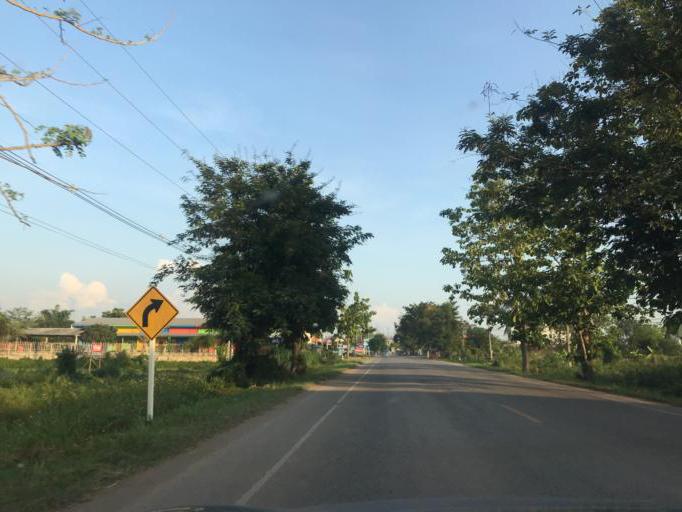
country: TH
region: Phayao
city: Chiang Kham
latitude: 19.5277
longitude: 100.2939
